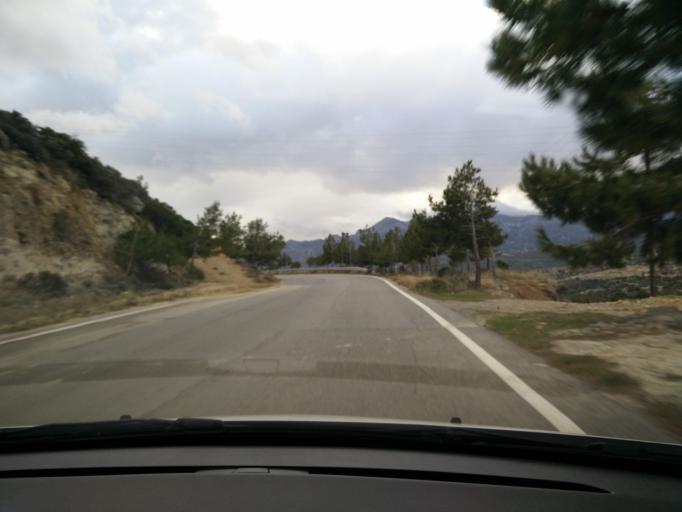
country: GR
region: Crete
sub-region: Nomos Lasithiou
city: Gra Liyia
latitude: 35.0786
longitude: 25.7063
